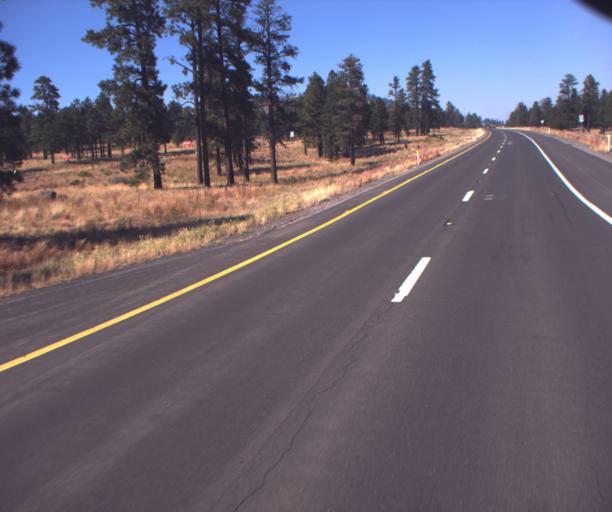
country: US
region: Arizona
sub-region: Coconino County
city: Flagstaff
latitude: 35.3725
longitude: -111.5754
